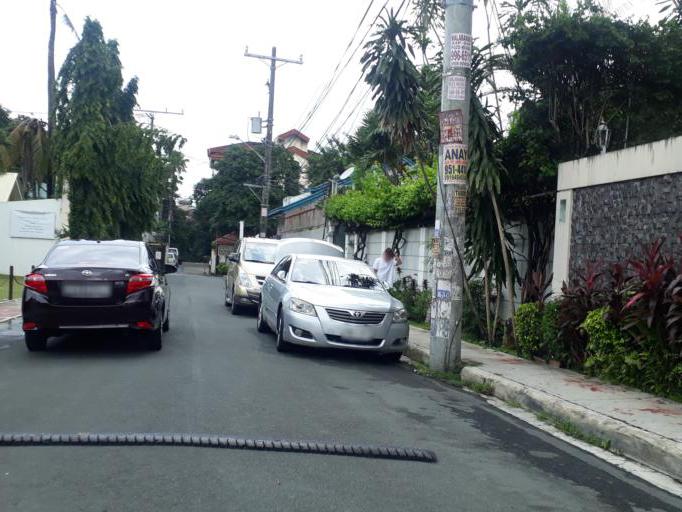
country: PH
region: Metro Manila
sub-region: San Juan
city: San Juan
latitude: 14.6222
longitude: 121.0408
